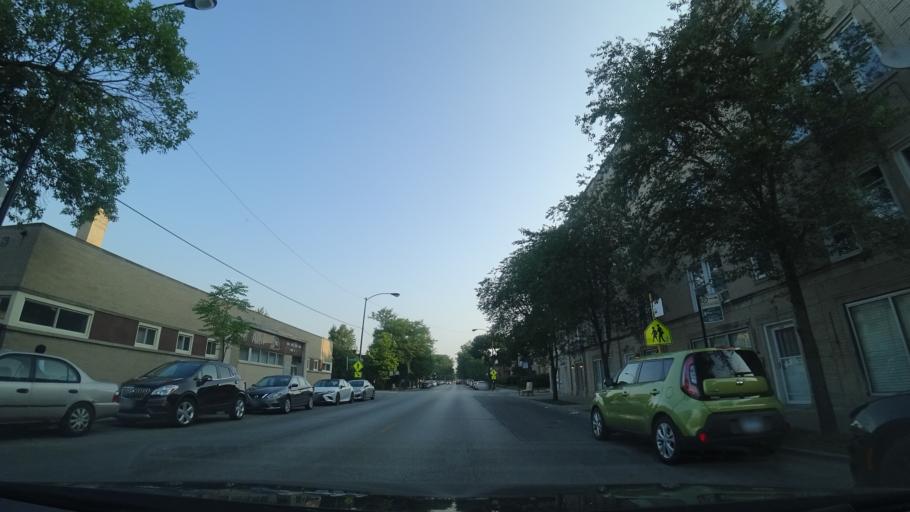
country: US
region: Illinois
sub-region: Cook County
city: Lincolnwood
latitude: 41.9987
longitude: -87.6998
